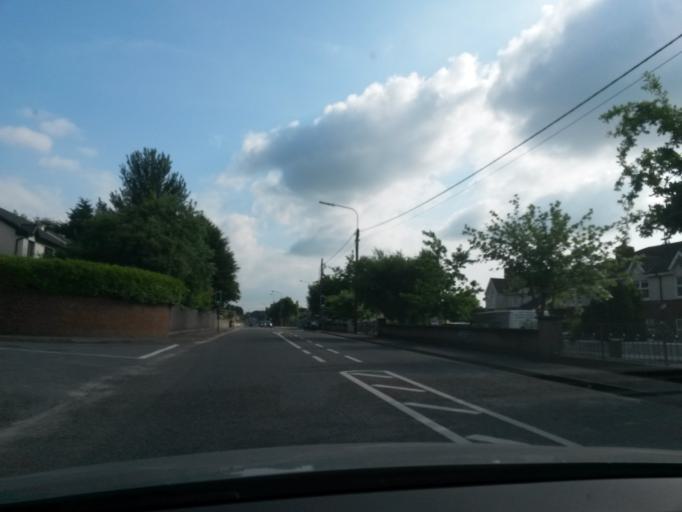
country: IE
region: Munster
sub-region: An Clar
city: Ennis
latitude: 52.8439
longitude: -8.9754
